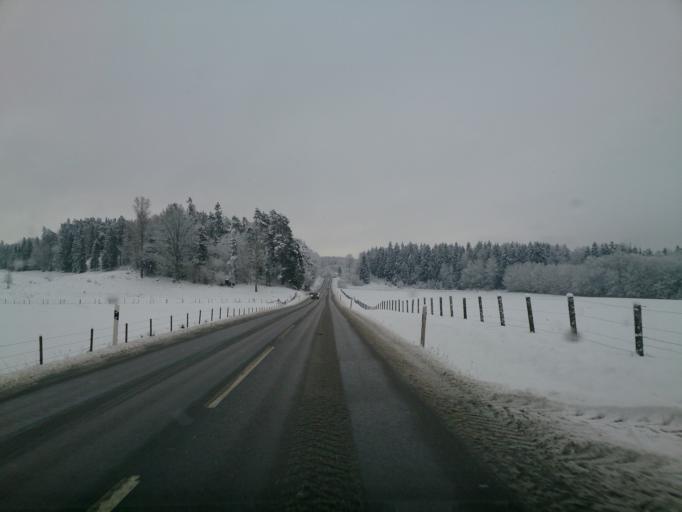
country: SE
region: OEstergoetland
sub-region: Atvidabergs Kommun
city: Atvidaberg
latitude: 58.2909
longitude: 15.8952
